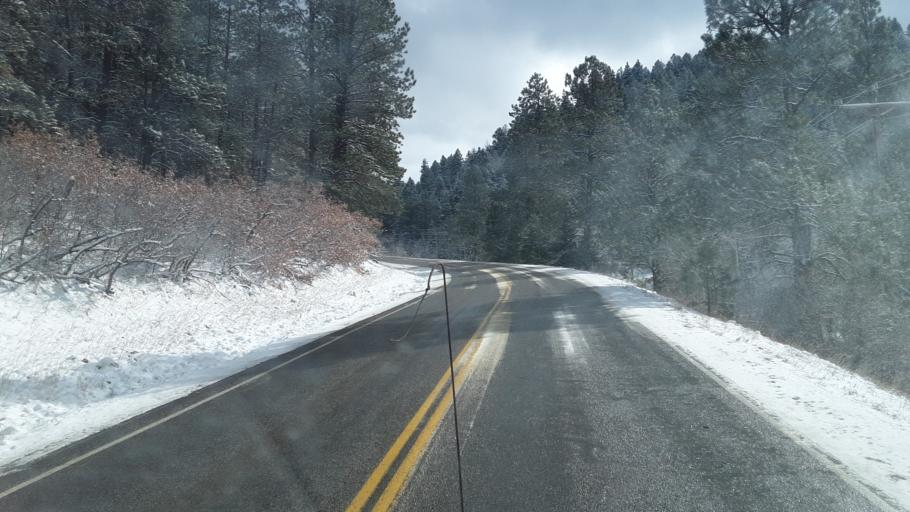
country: US
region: Colorado
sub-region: La Plata County
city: Bayfield
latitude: 37.3581
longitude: -107.6683
